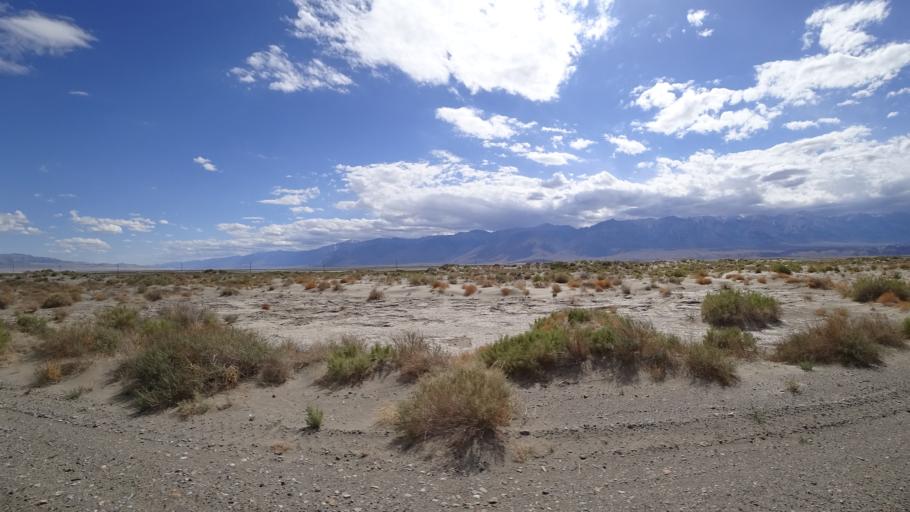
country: US
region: California
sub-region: Inyo County
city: Lone Pine
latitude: 36.5386
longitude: -117.9284
